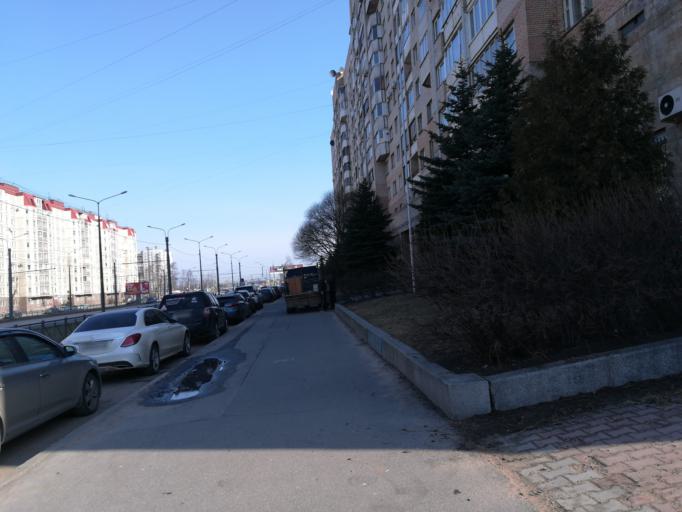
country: RU
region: St.-Petersburg
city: Vasyl'evsky Ostrov
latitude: 59.9525
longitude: 30.2349
